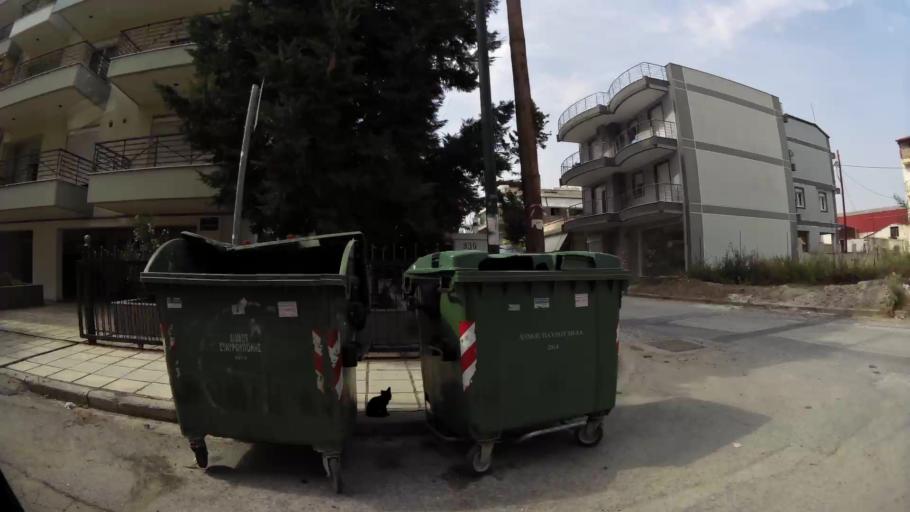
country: GR
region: Central Macedonia
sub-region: Nomos Thessalonikis
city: Stavroupoli
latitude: 40.6851
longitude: 22.9342
